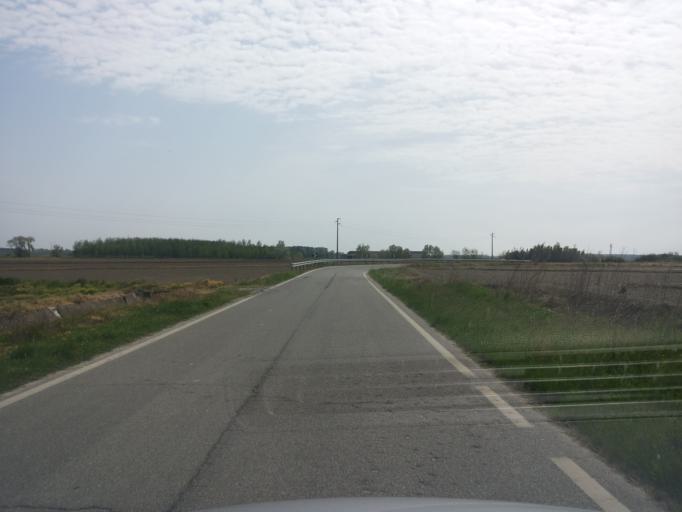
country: IT
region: Piedmont
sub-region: Provincia di Vercelli
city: Caresana
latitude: 45.2082
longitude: 8.5125
